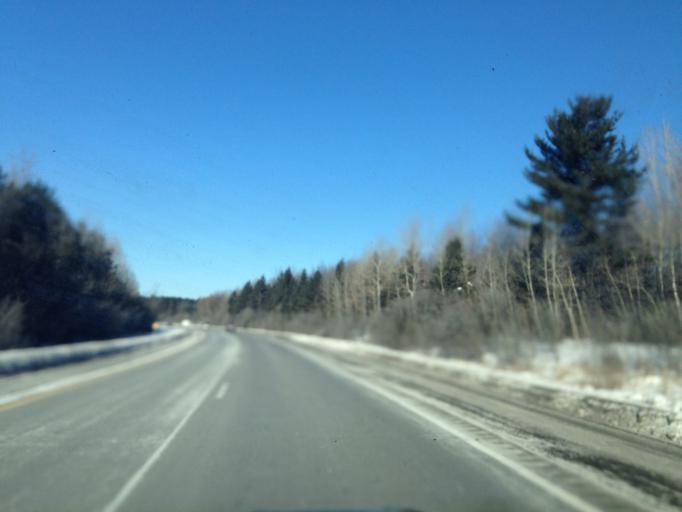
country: CA
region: Ontario
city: Ottawa
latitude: 45.3618
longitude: -75.4797
